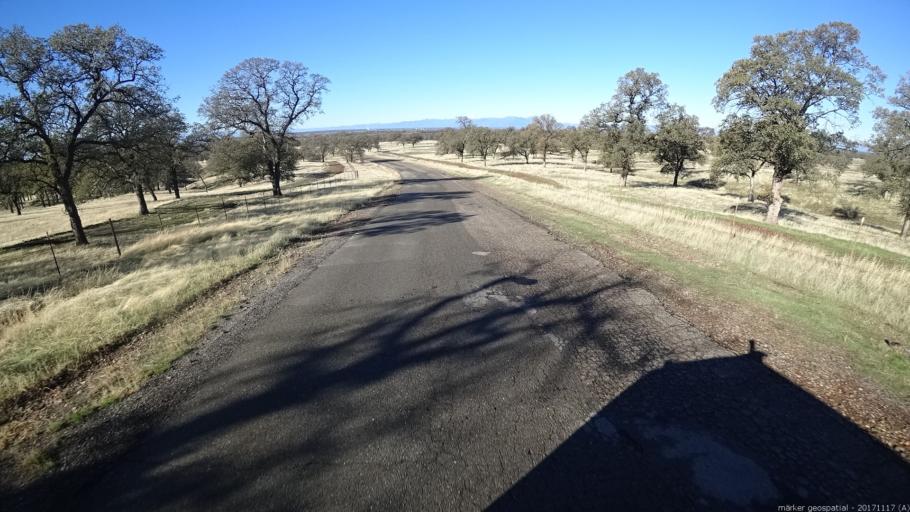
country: US
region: California
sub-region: Shasta County
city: Cottonwood
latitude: 40.4254
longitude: -122.1798
